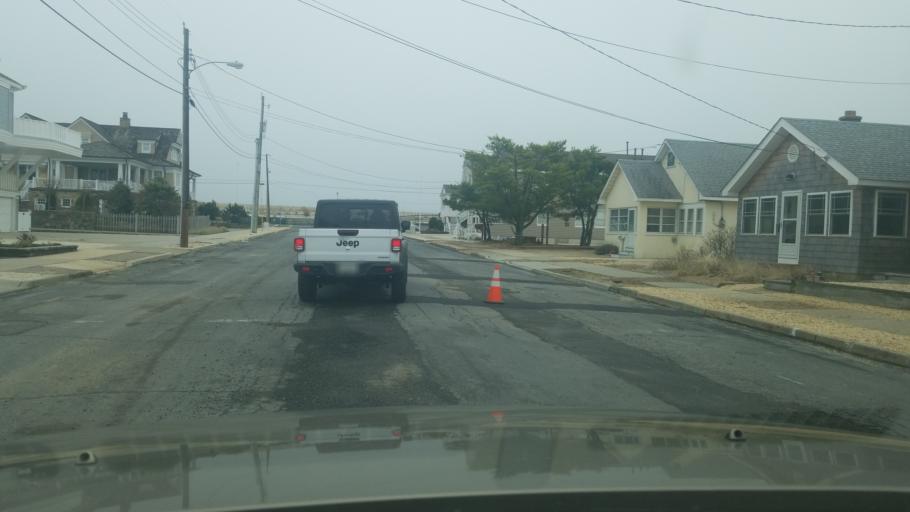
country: US
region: New Jersey
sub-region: Ocean County
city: Seaside Park
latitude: 39.9136
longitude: -74.0785
